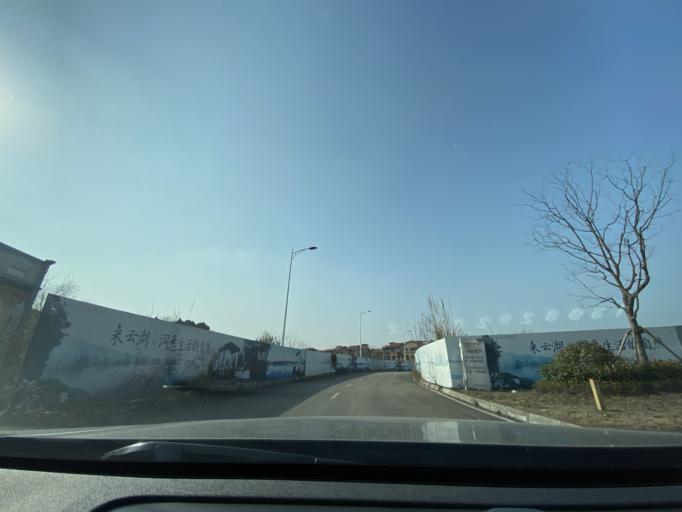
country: CN
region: Sichuan
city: Wenlin
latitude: 30.2520
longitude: 104.2472
